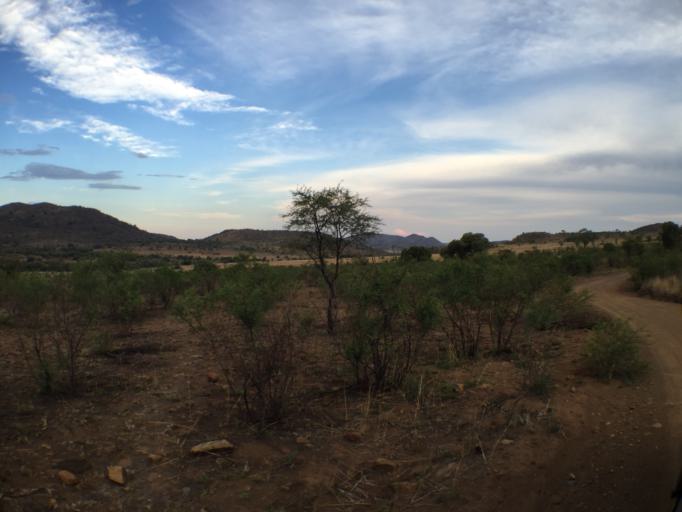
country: ZA
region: North-West
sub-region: Bojanala Platinum District Municipality
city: Mogwase
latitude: -25.2246
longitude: 27.0701
